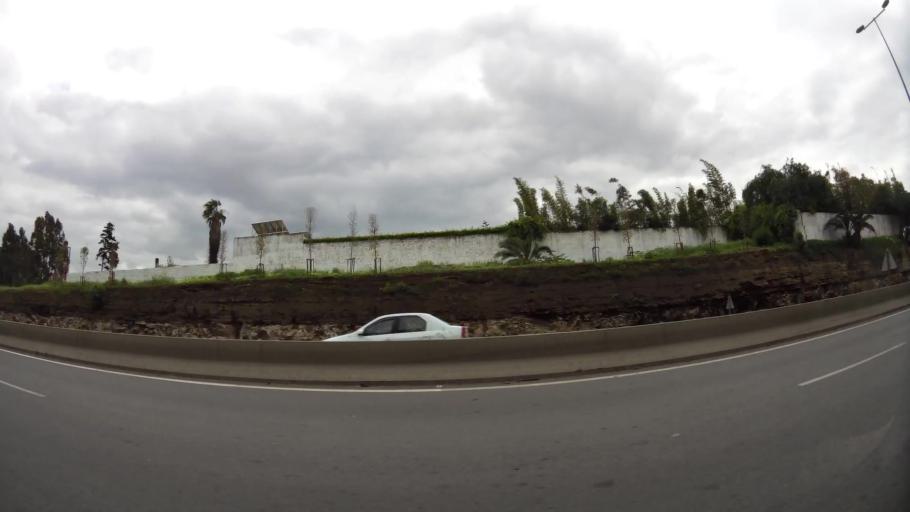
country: MA
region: Grand Casablanca
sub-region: Casablanca
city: Casablanca
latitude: 33.5551
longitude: -7.6164
